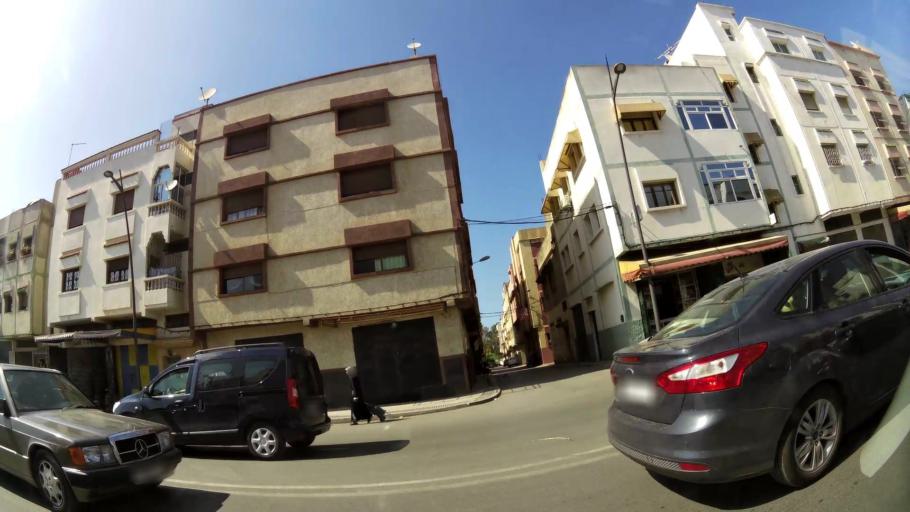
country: MA
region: Rabat-Sale-Zemmour-Zaer
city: Sale
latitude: 34.0467
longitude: -6.7752
